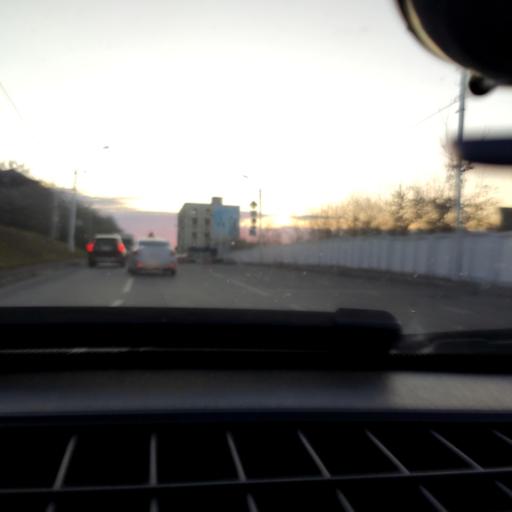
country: RU
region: Bashkortostan
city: Ufa
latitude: 54.7467
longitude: 55.9452
